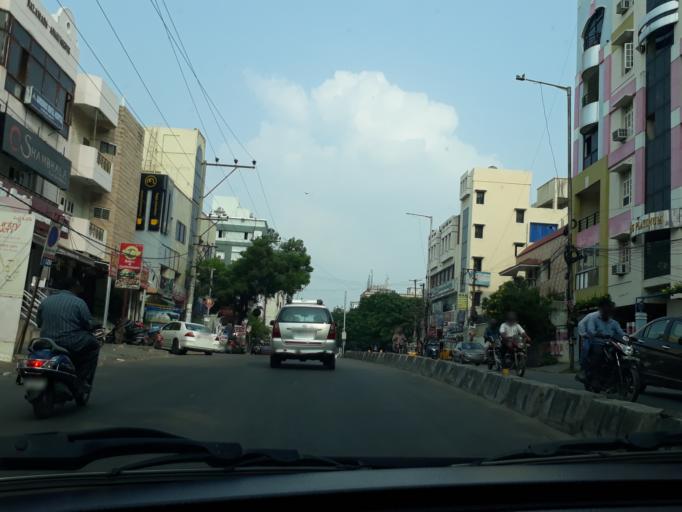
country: IN
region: Telangana
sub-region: Hyderabad
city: Hyderabad
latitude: 17.4302
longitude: 78.4381
